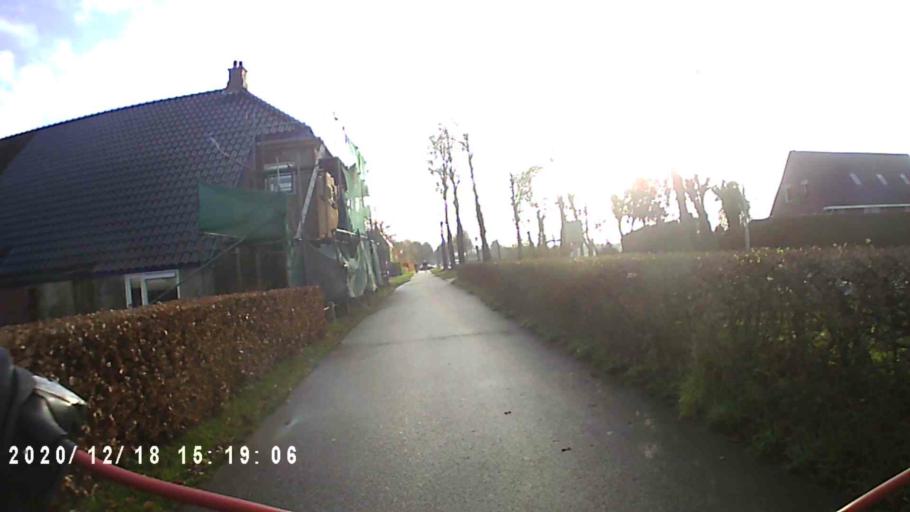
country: NL
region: Groningen
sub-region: Gemeente Hoogezand-Sappemeer
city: Hoogezand
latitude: 53.1589
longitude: 6.7229
